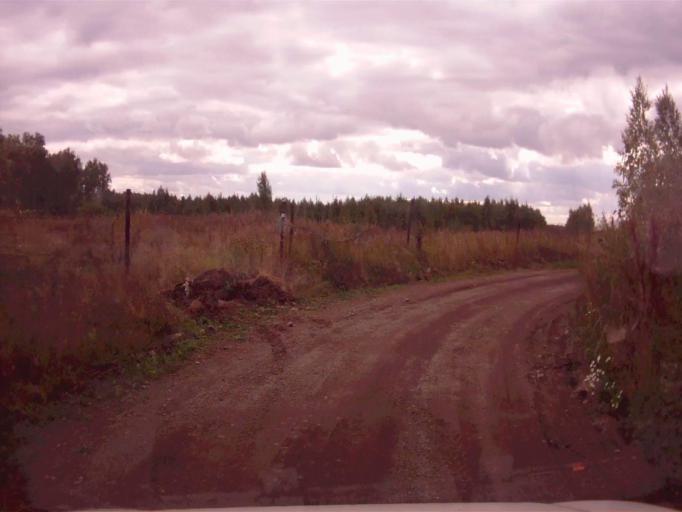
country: RU
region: Chelyabinsk
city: Sargazy
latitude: 55.1263
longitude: 61.2504
